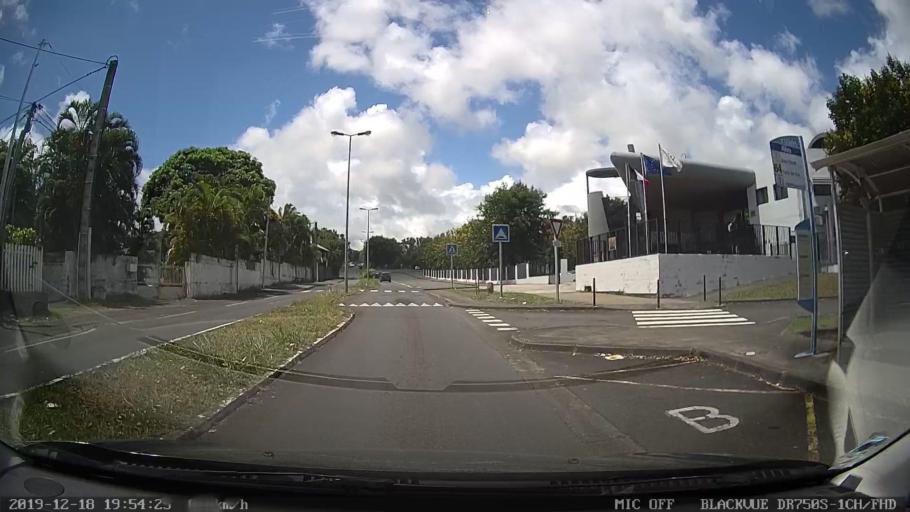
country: RE
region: Reunion
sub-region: Reunion
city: Saint-Andre
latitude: -20.9332
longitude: 55.6381
